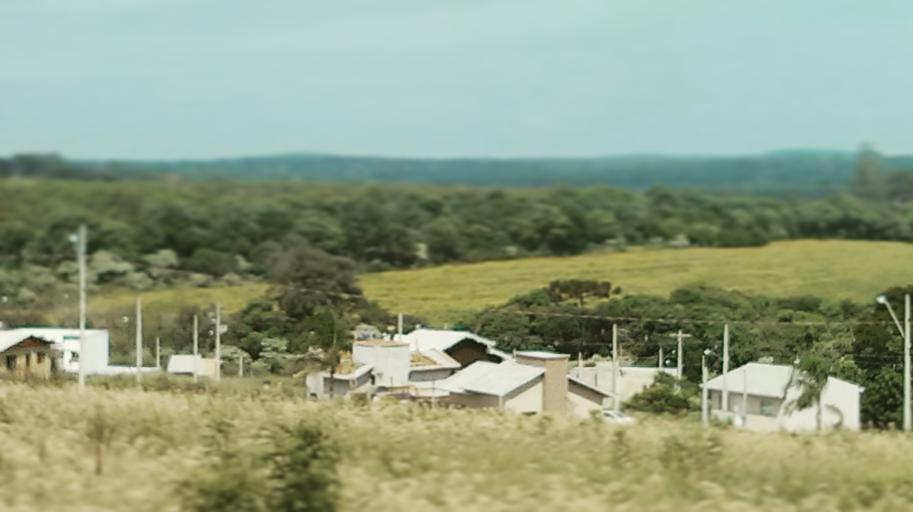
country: BR
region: Santa Catarina
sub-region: Chapeco
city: Chapeco
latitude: -27.0889
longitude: -52.7136
